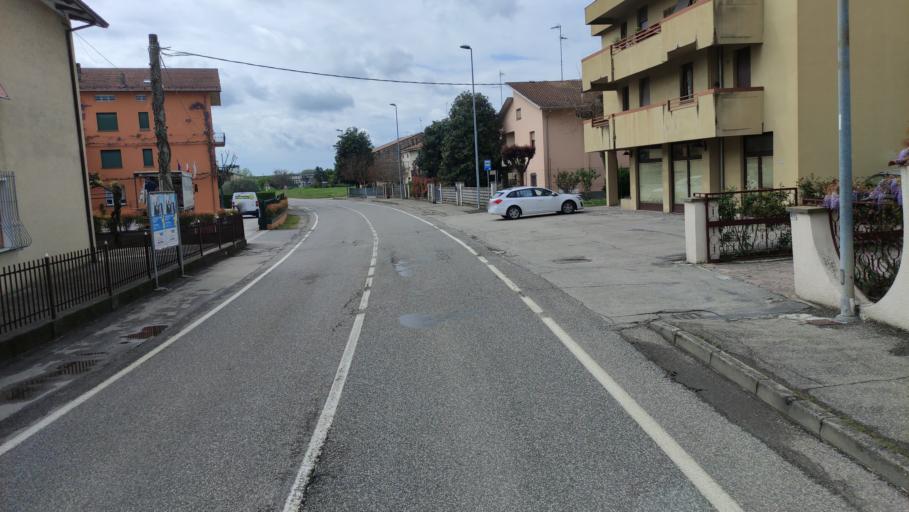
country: IT
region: Emilia-Romagna
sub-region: Provincia di Parma
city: Colorno
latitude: 44.9311
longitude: 10.3632
